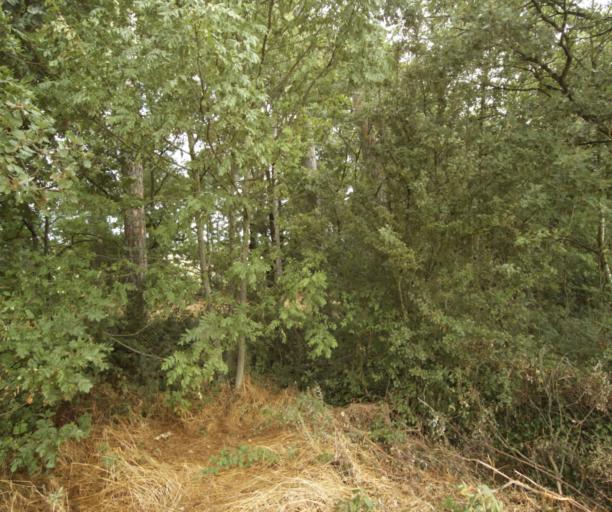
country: FR
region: Midi-Pyrenees
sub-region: Departement de la Haute-Garonne
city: Revel
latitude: 43.4433
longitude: 1.9562
